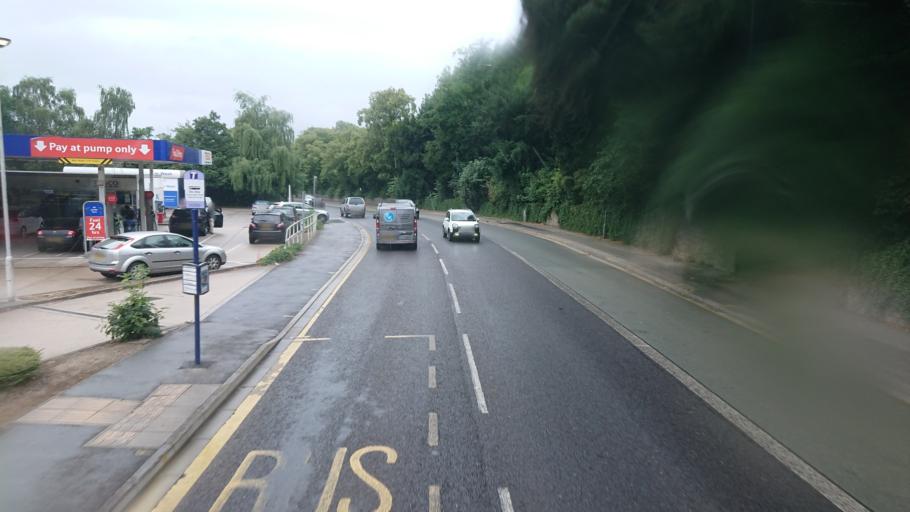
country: GB
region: England
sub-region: Sheffield
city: Sheffield
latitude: 53.3486
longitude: -1.4931
